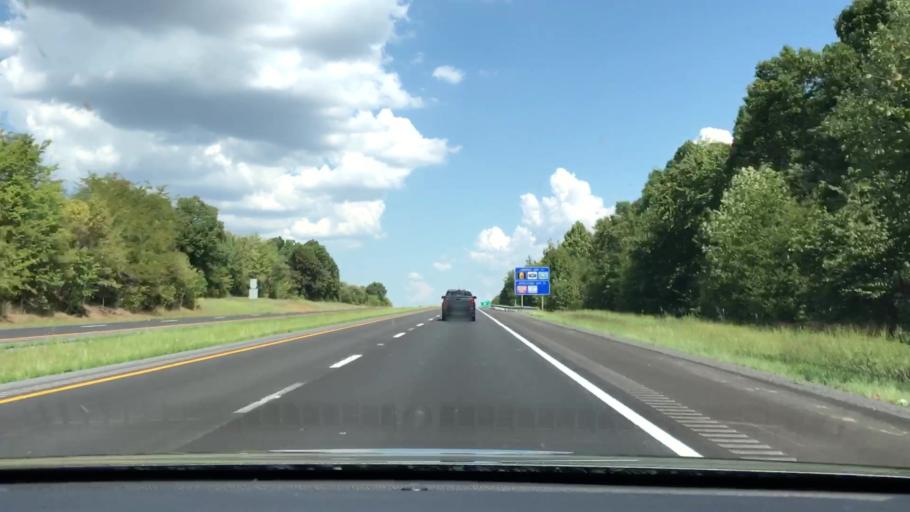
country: US
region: Kentucky
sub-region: Lyon County
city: Eddyville
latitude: 37.0991
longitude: -88.0394
